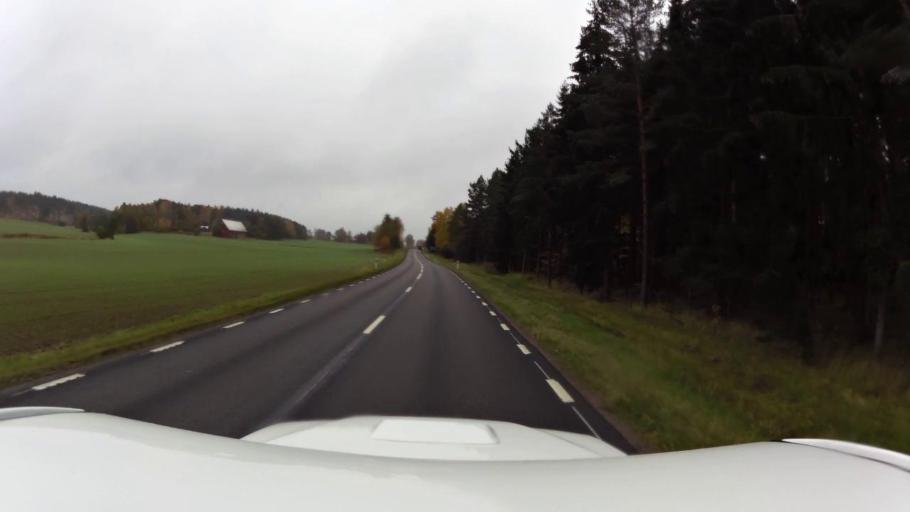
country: SE
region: OEstergoetland
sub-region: Linkopings Kommun
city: Linghem
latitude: 58.3622
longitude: 15.8255
